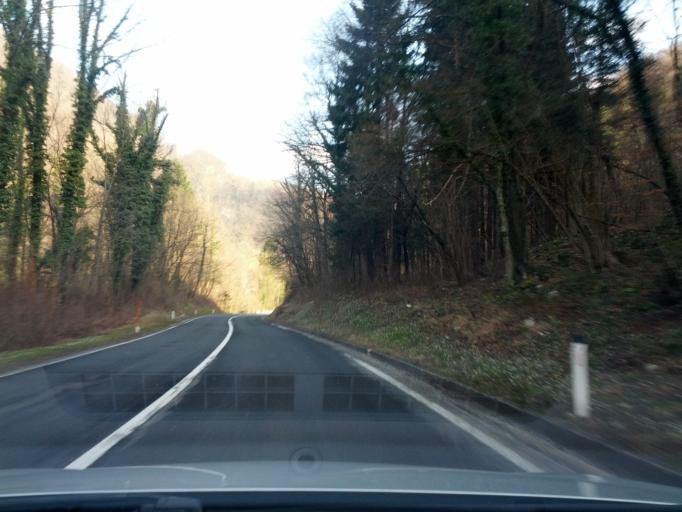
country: SI
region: Zagorje ob Savi
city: Kisovec
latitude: 46.0979
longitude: 14.9583
